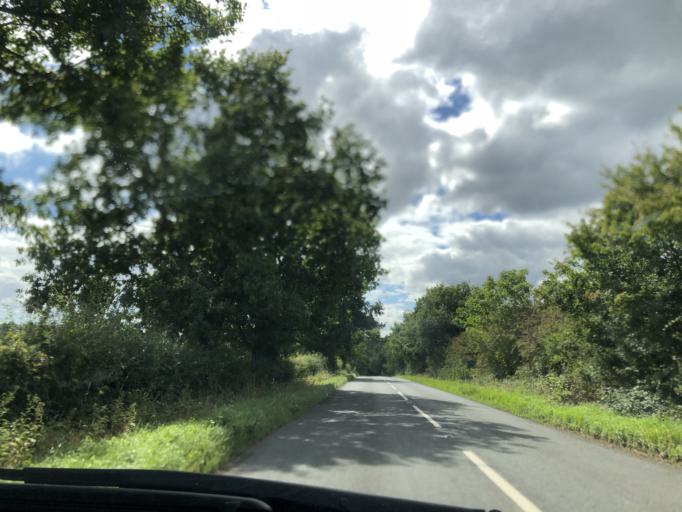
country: GB
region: England
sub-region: Kent
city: Halstead
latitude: 51.2840
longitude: 0.1290
